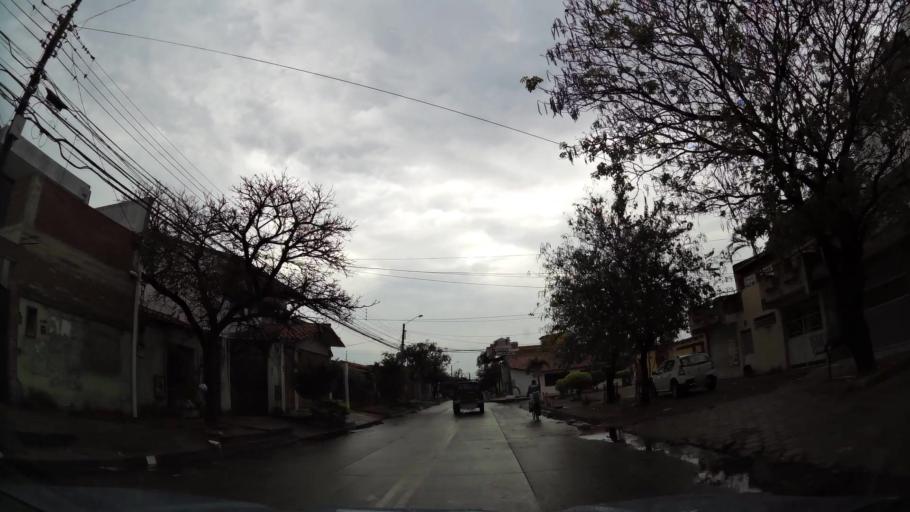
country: BO
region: Santa Cruz
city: Santa Cruz de la Sierra
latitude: -17.7614
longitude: -63.1552
